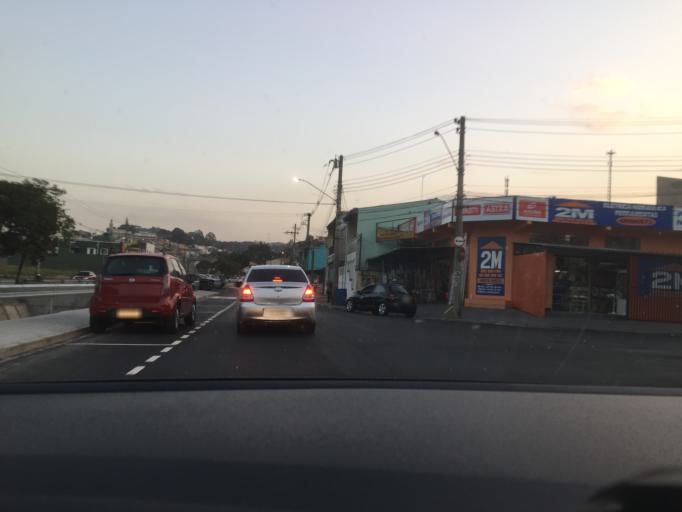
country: BR
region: Sao Paulo
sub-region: Varzea Paulista
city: Varzea Paulista
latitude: -23.2223
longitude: -46.8413
